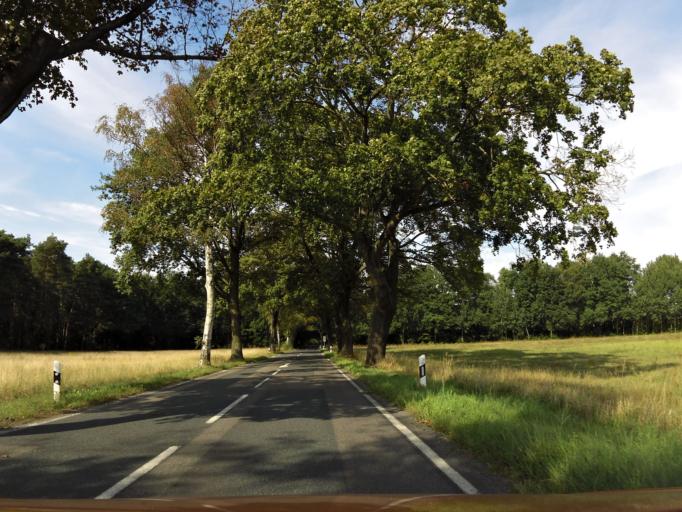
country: DE
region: Brandenburg
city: Michendorf
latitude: 52.2848
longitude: 13.1138
